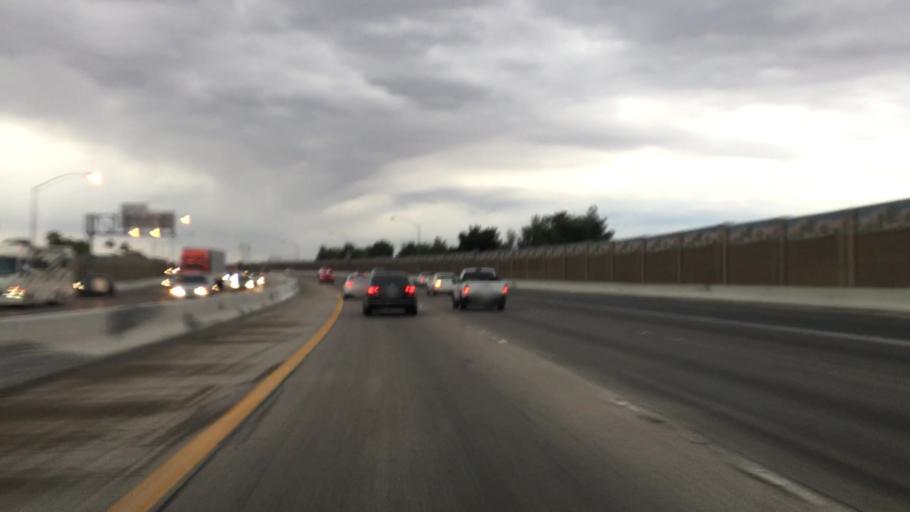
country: US
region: Nevada
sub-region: Clark County
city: Winchester
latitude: 36.1628
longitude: -115.0927
